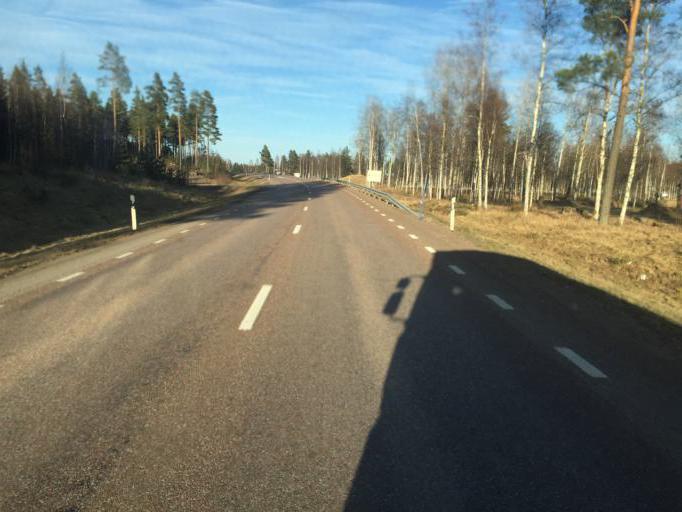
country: SE
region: Dalarna
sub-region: Gagnefs Kommun
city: Mockfjard
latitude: 60.5324
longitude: 15.0357
